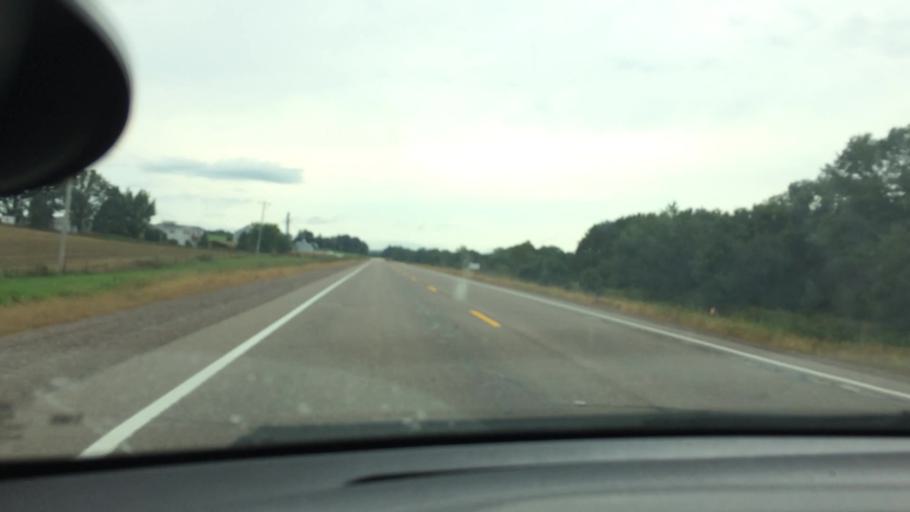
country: US
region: Wisconsin
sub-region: Trempealeau County
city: Osseo
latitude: 44.5882
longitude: -91.1575
